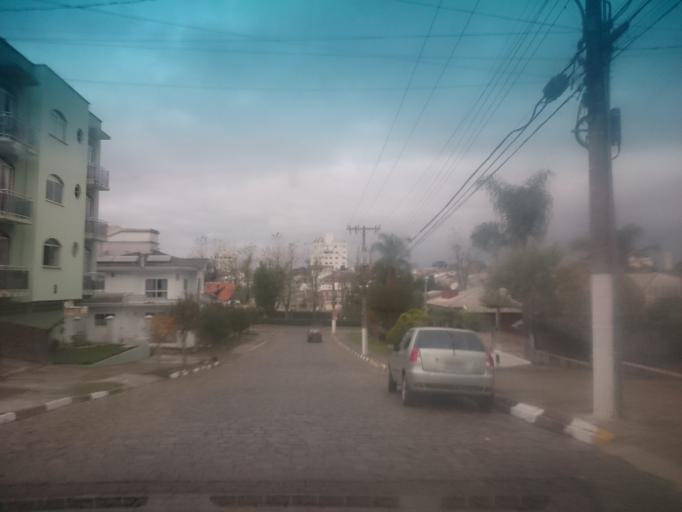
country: BR
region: Santa Catarina
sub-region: Lages
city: Lages
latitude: -27.8185
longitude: -50.3212
